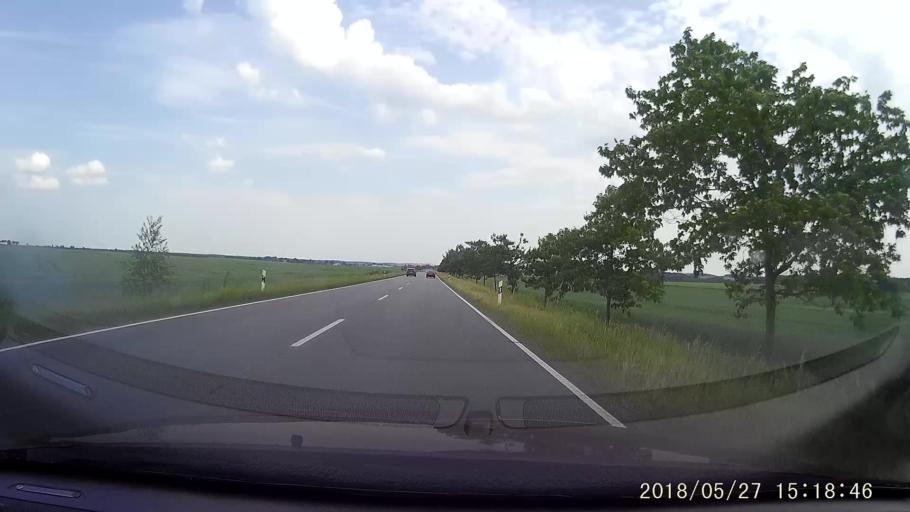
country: DE
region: Saxony
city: Kodersdorf
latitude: 51.2622
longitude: 14.8618
